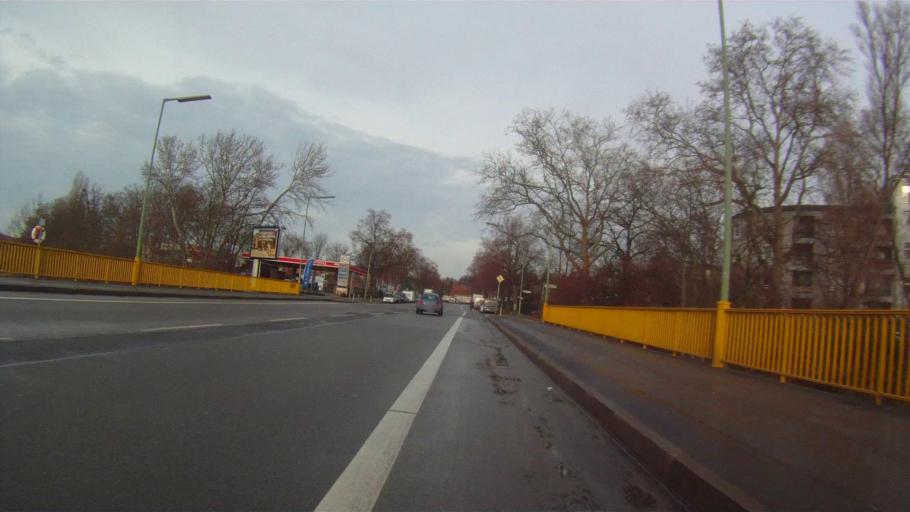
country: DE
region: Berlin
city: Britz
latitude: 52.4565
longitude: 13.4271
